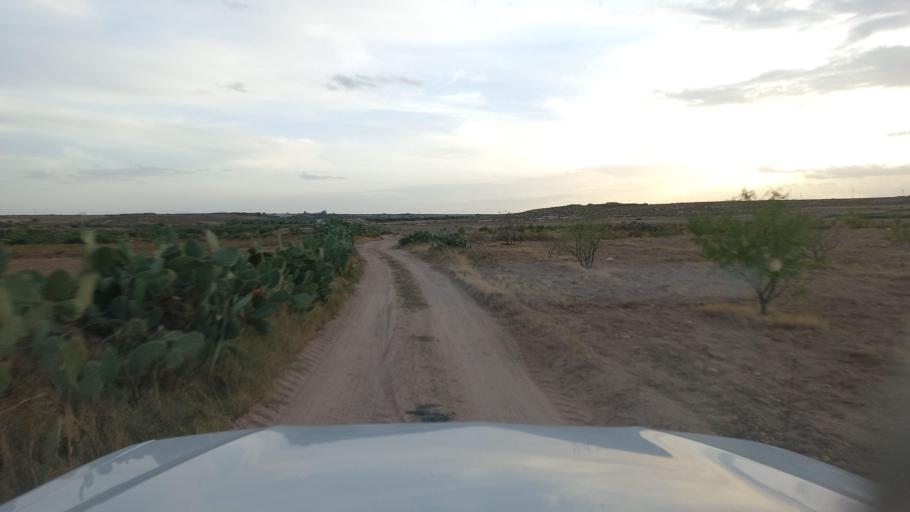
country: TN
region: Al Qasrayn
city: Sbiba
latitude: 35.4147
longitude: 9.0853
